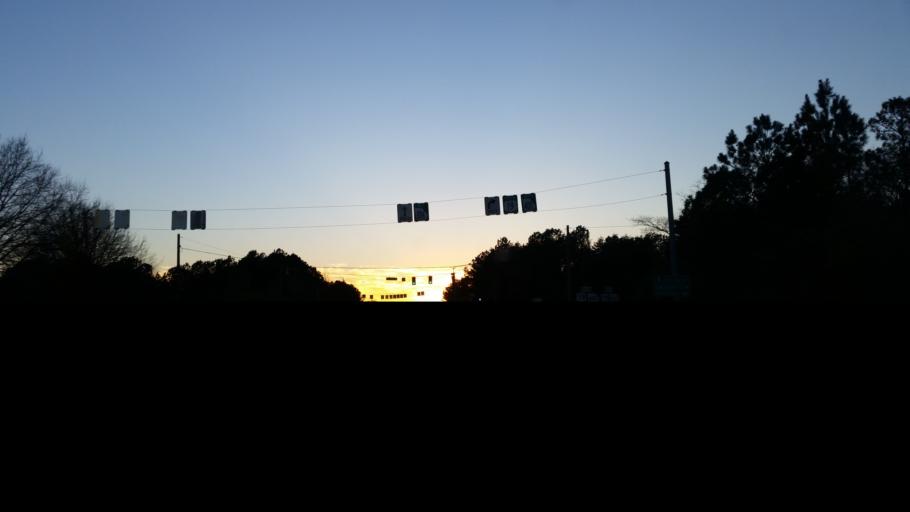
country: US
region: Georgia
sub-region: Forsyth County
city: Cumming
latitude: 34.2526
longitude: -84.0906
